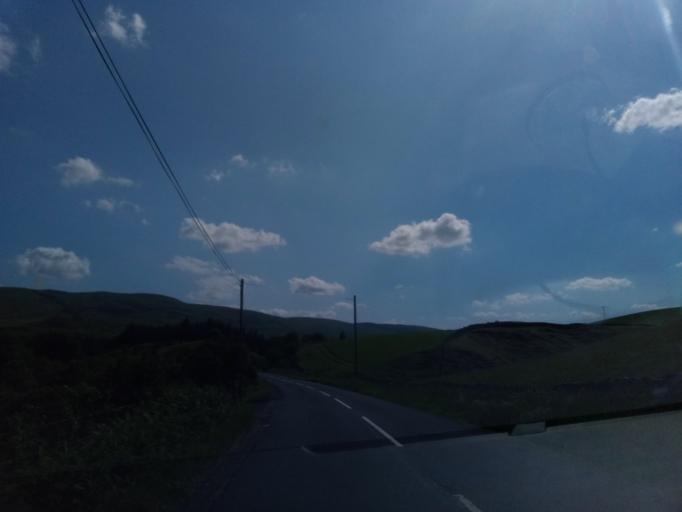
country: GB
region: Scotland
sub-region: The Scottish Borders
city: Innerleithen
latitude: 55.5298
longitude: -3.0389
